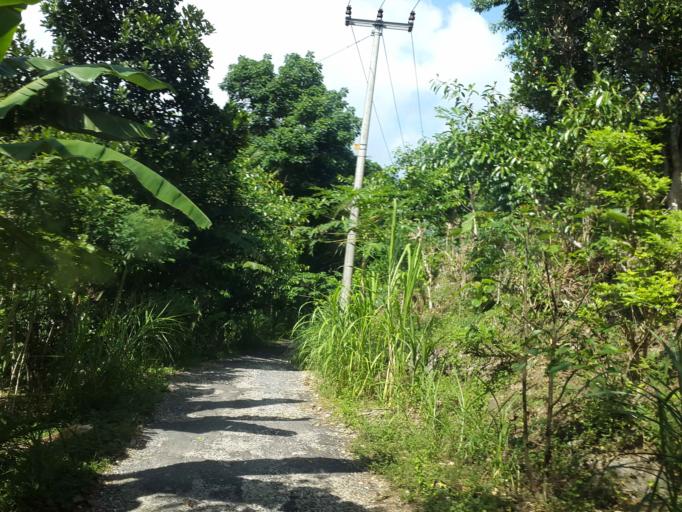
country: ID
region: Bali
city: Tanjung
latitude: -8.7768
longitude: 115.5229
